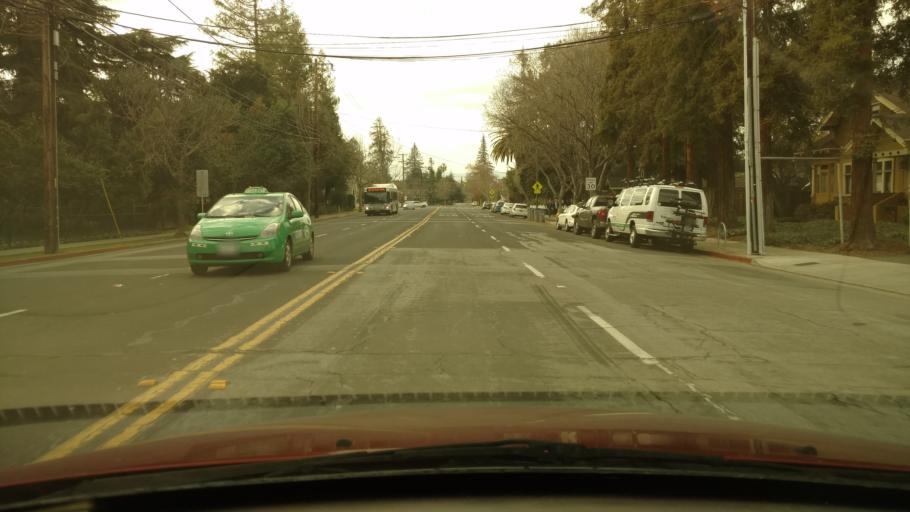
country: US
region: California
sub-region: Santa Clara County
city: Buena Vista
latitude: 37.3025
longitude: -121.8997
